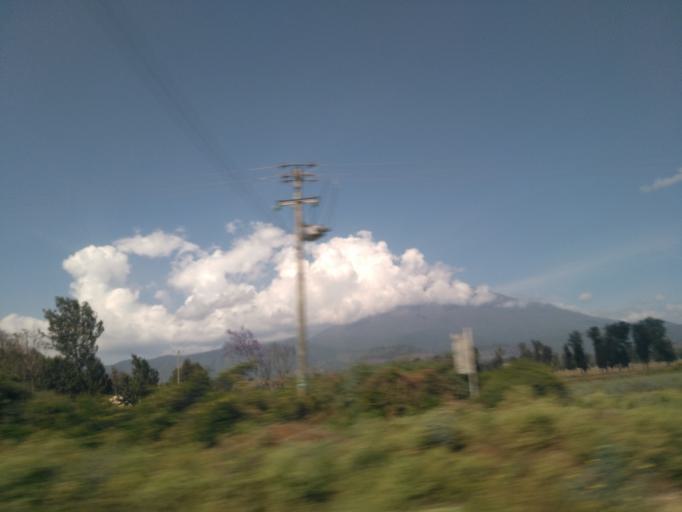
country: TZ
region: Arusha
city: Arusha
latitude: -3.3038
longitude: 36.6331
